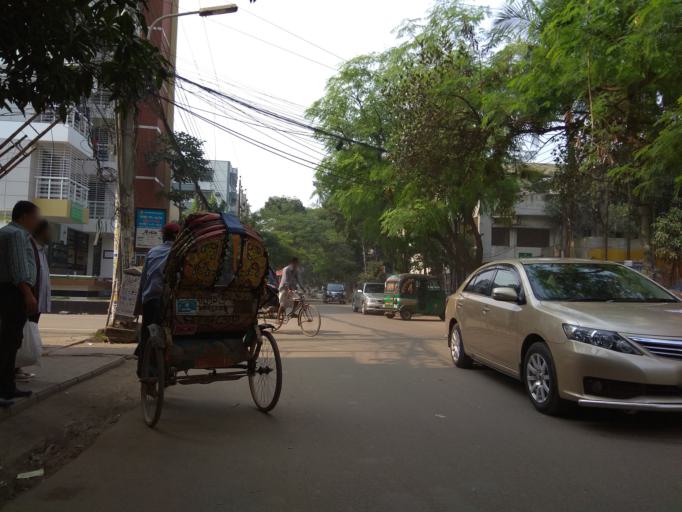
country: BD
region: Dhaka
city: Tungi
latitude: 23.8645
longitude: 90.3904
